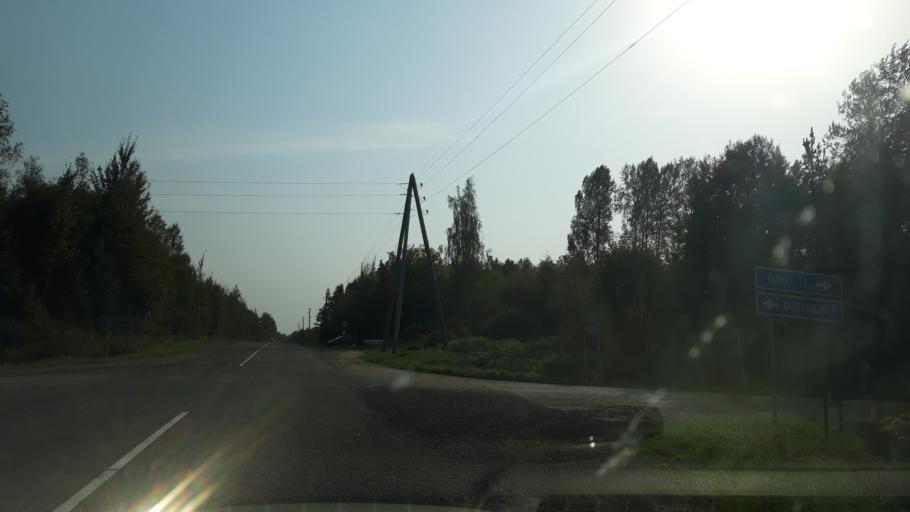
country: LV
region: Burtnieki
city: Matisi
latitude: 57.6384
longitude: 25.2525
